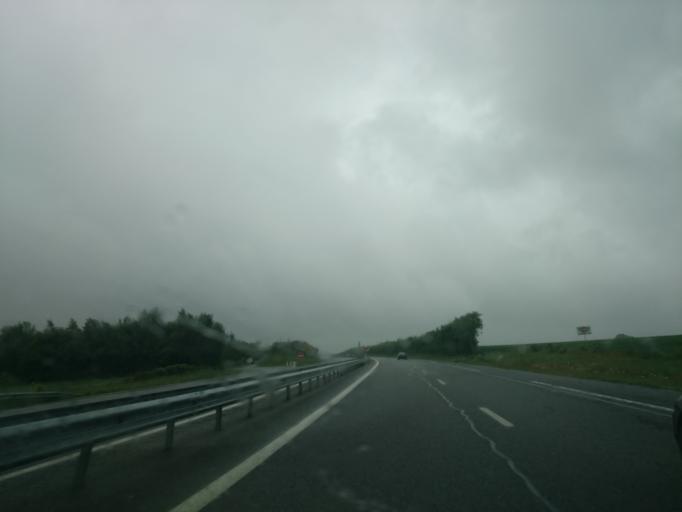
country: FR
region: Brittany
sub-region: Departement d'Ille-et-Vilaine
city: Plelan-le-Grand
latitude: 47.9751
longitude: -2.0978
